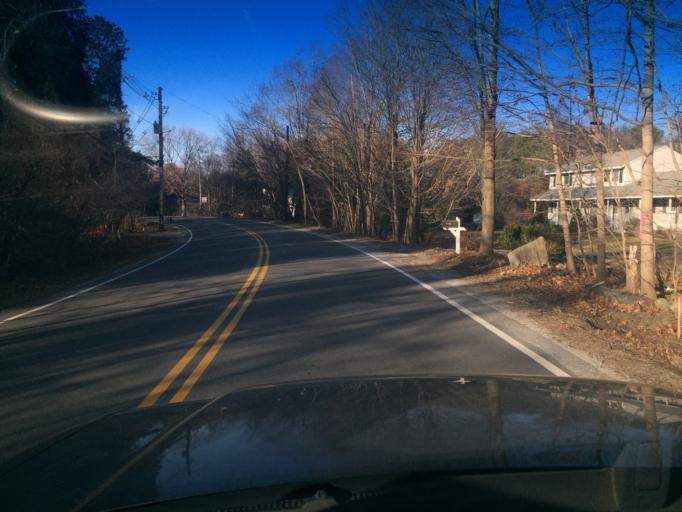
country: US
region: Massachusetts
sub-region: Middlesex County
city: Sherborn
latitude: 42.2670
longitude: -71.3804
